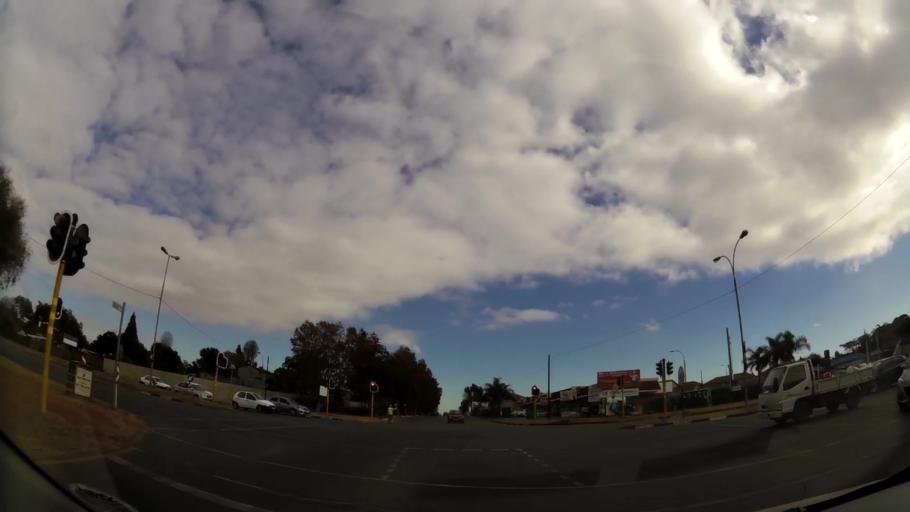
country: ZA
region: Gauteng
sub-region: City of Johannesburg Metropolitan Municipality
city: Roodepoort
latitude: -26.1093
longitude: 27.8558
